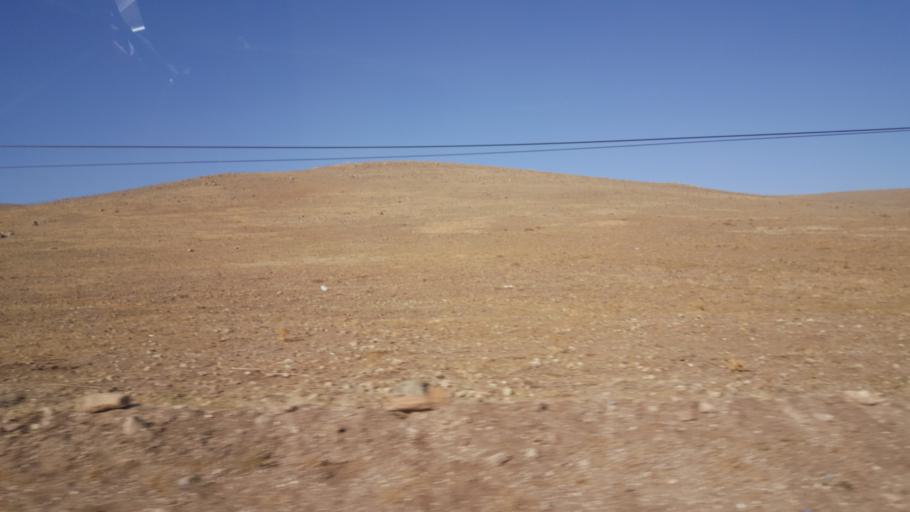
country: TR
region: Ankara
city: Altpinar
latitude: 39.1707
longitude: 32.6977
